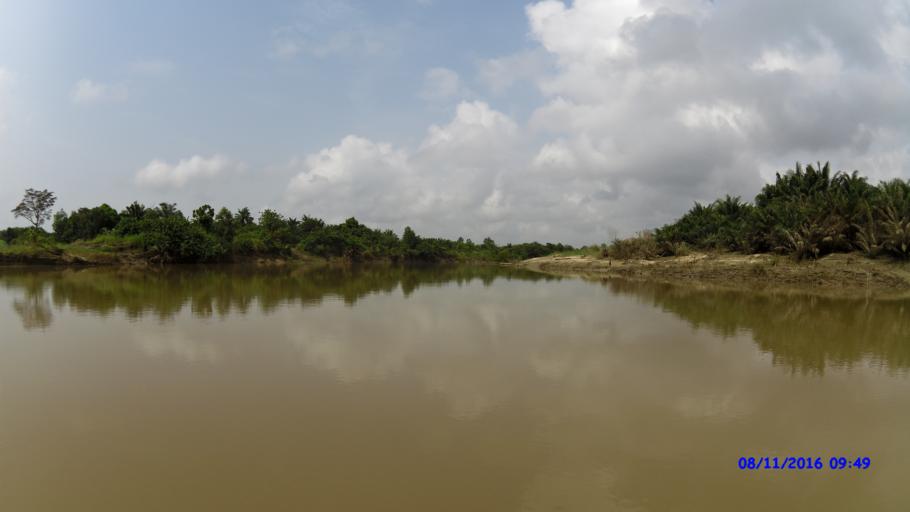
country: BJ
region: Mono
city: Come
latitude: 6.4306
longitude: 1.7693
